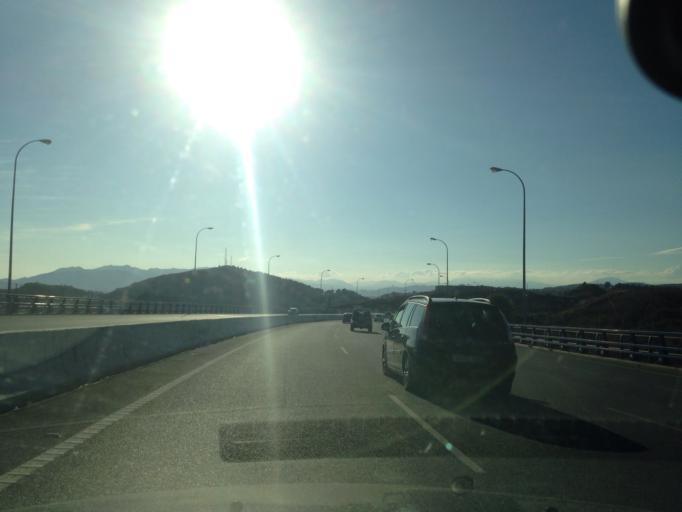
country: ES
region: Andalusia
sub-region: Provincia de Malaga
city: Malaga
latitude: 36.7388
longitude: -4.3900
